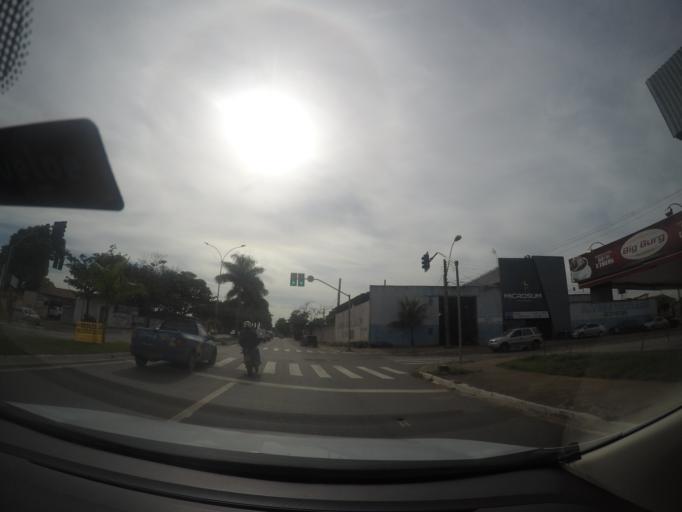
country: BR
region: Goias
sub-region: Goiania
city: Goiania
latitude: -16.6635
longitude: -49.2879
